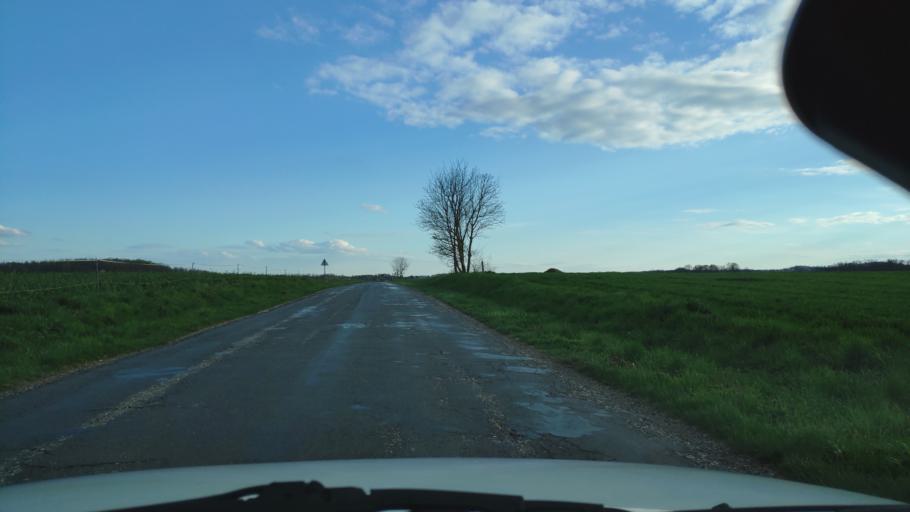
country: HU
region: Zala
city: Zalakomar
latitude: 46.4780
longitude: 17.1280
